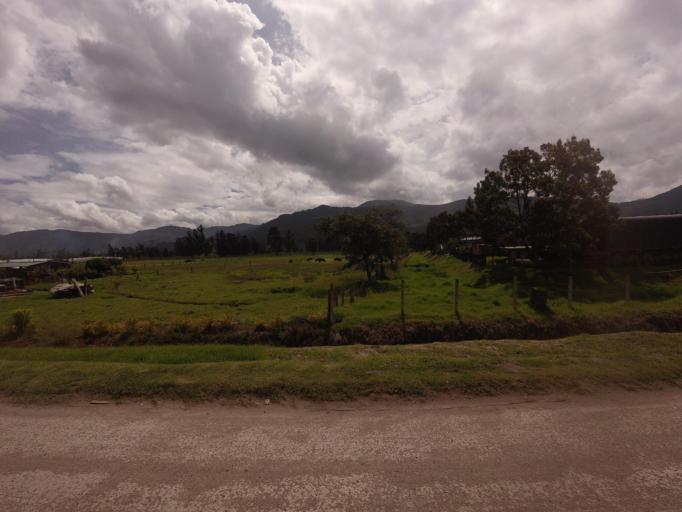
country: CO
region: Boyaca
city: Tibasosa
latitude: 5.7898
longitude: -72.9858
